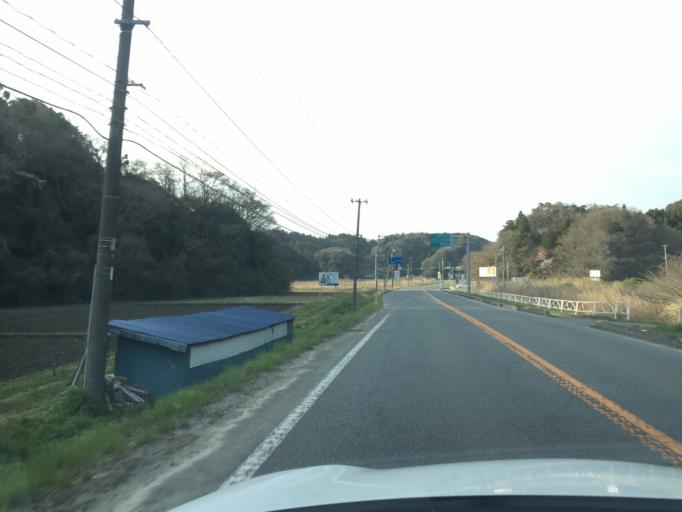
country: JP
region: Fukushima
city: Iwaki
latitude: 37.0032
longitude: 140.9671
